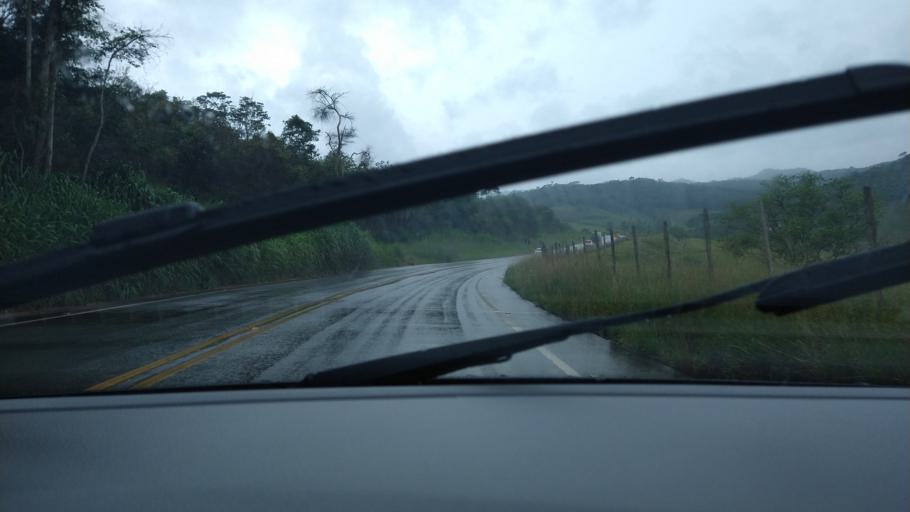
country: BR
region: Minas Gerais
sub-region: Vicosa
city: Vicosa
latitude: -20.6086
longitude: -42.8682
